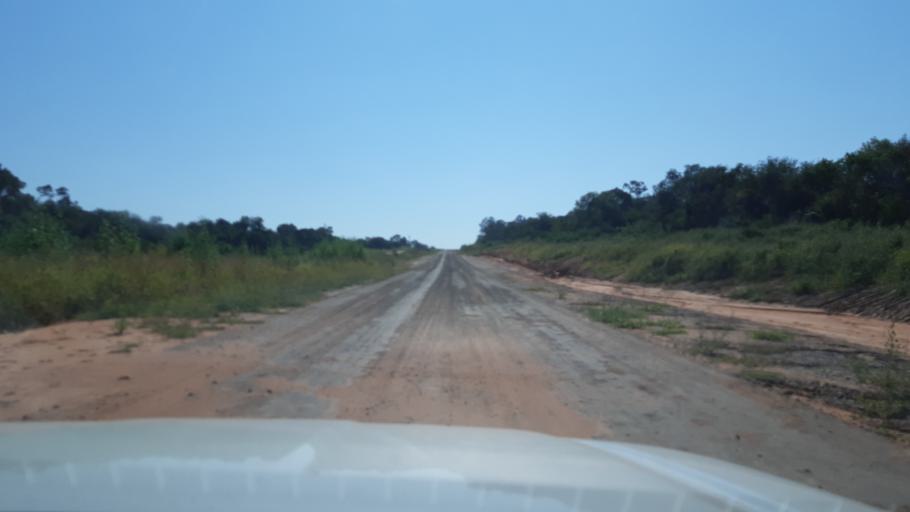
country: AR
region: Jujuy
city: La Mendieta
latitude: -24.4056
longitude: -64.9932
